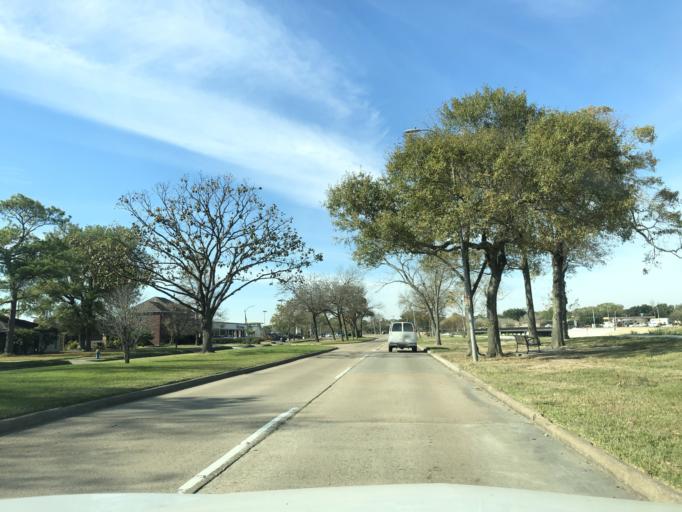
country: US
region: Texas
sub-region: Harris County
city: Bellaire
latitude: 29.6766
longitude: -95.4910
